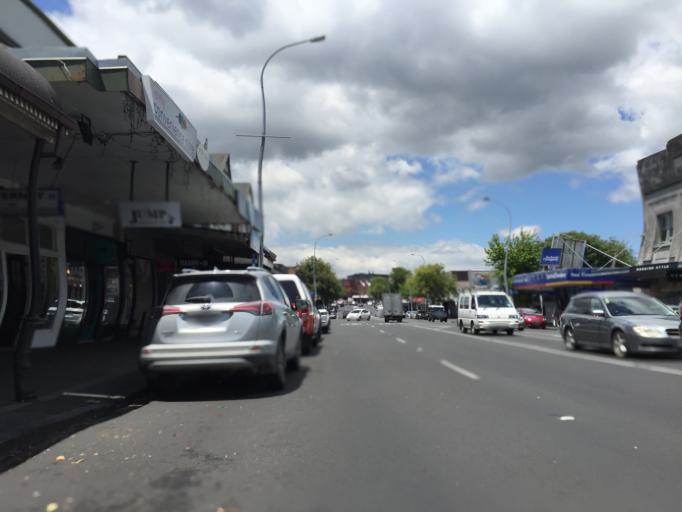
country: NZ
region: Auckland
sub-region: Auckland
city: Auckland
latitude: -36.8536
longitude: 174.7456
